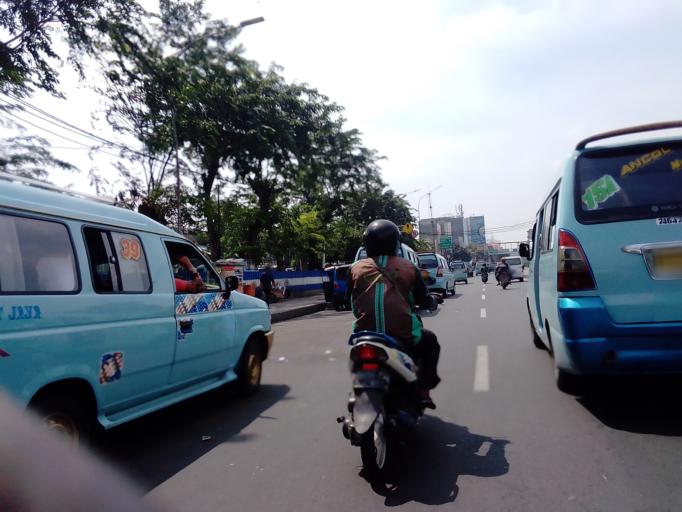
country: ID
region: Jakarta Raya
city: Jakarta
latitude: -6.1380
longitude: 106.8157
